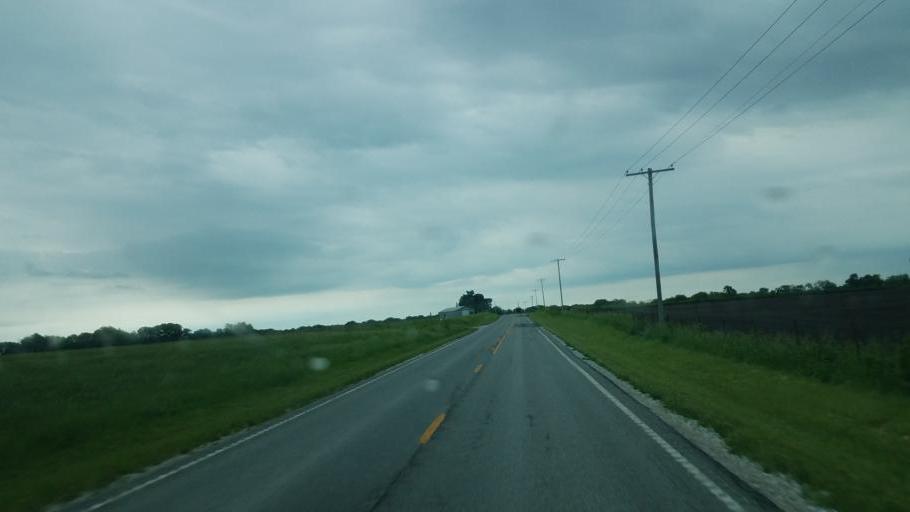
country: US
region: Missouri
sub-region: Moniteau County
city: California
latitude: 38.8245
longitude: -92.6055
